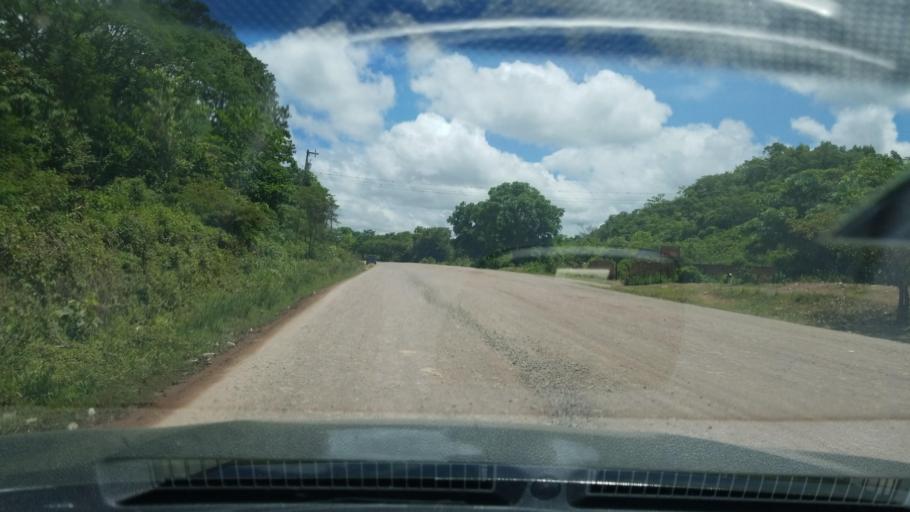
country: HN
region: Francisco Morazan
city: Talanga
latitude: 14.3548
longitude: -87.0445
